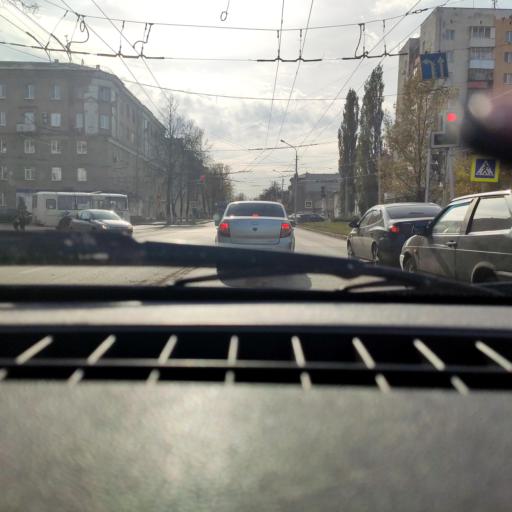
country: RU
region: Bashkortostan
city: Ufa
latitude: 54.8225
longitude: 56.0793
